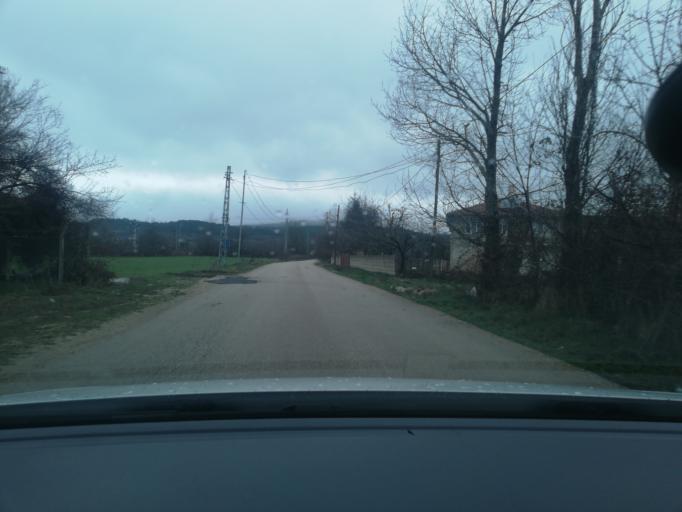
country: TR
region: Bolu
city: Bolu
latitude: 40.7311
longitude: 31.5448
